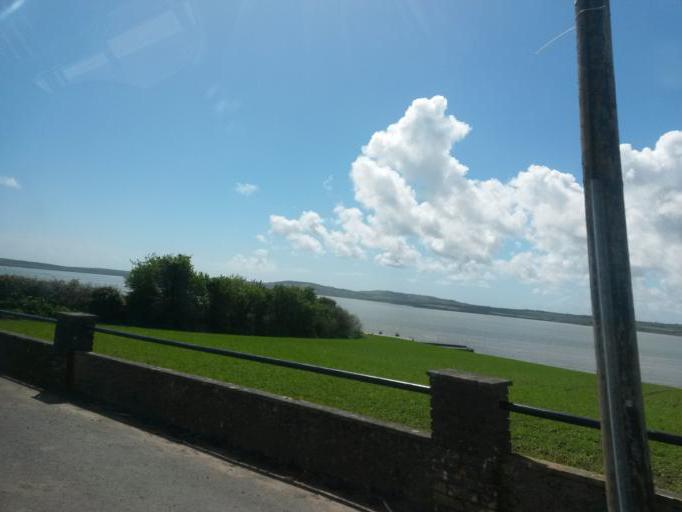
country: IE
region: Munster
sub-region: Waterford
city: Dunmore East
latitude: 52.2242
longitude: -6.9323
